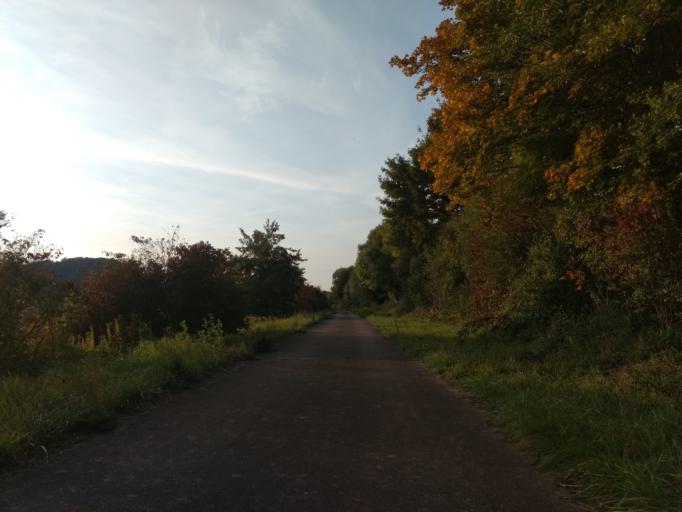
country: DE
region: Saarland
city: Wallerfangen
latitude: 49.3313
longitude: 6.7342
